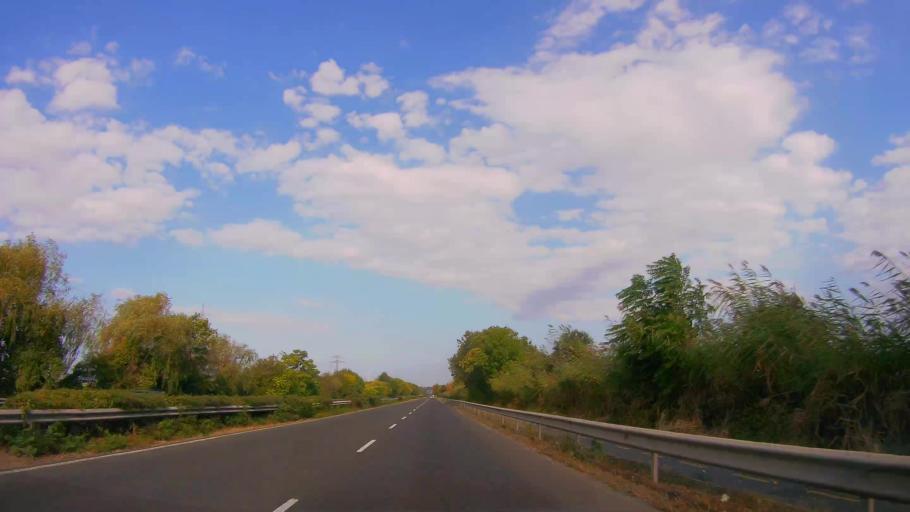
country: BG
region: Burgas
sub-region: Obshtina Burgas
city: Burgas
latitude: 42.4467
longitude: 27.4584
